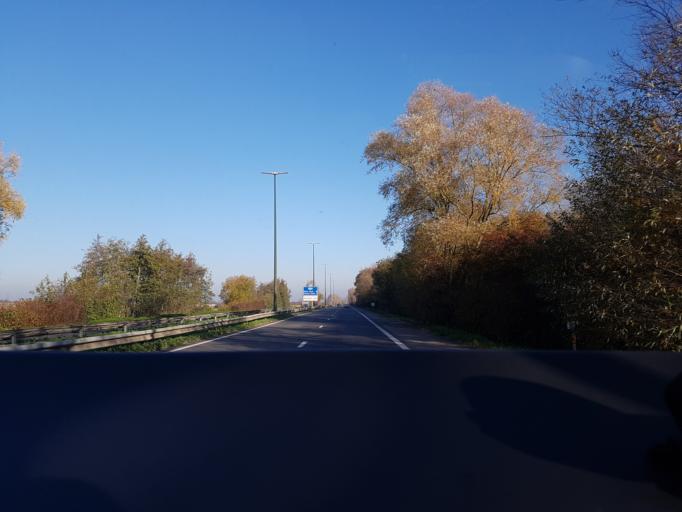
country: FR
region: Nord-Pas-de-Calais
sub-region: Departement du Nord
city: Deulemont
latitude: 50.7444
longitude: 2.9317
